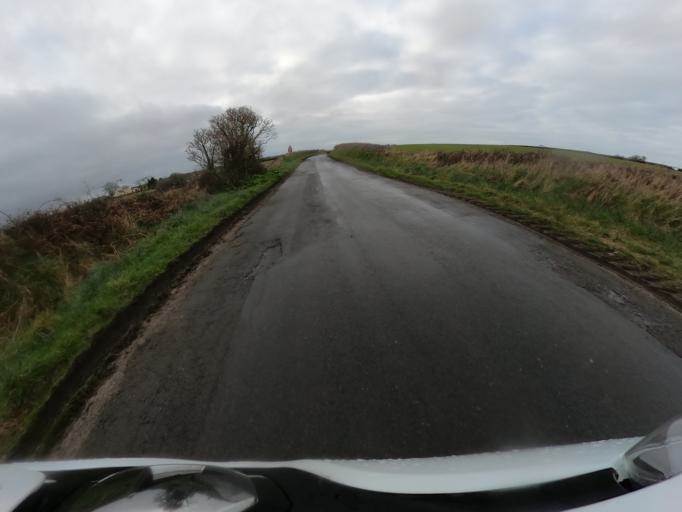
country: IM
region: Ramsey
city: Ramsey
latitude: 54.3632
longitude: -4.4644
